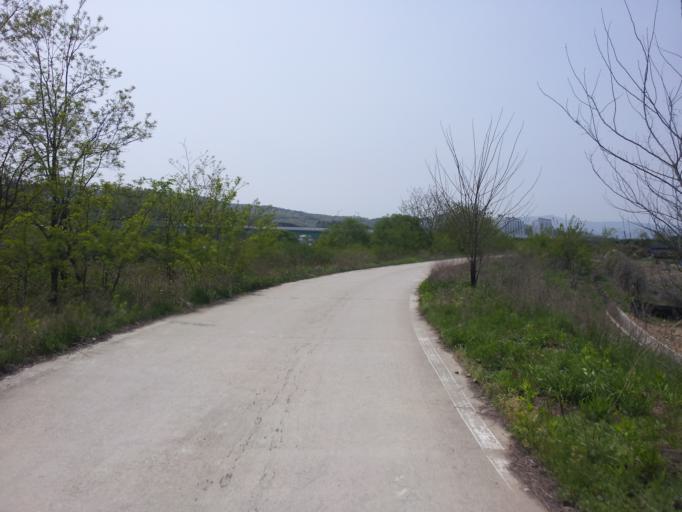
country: KR
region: Daejeon
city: Daejeon
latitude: 36.2653
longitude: 127.2829
